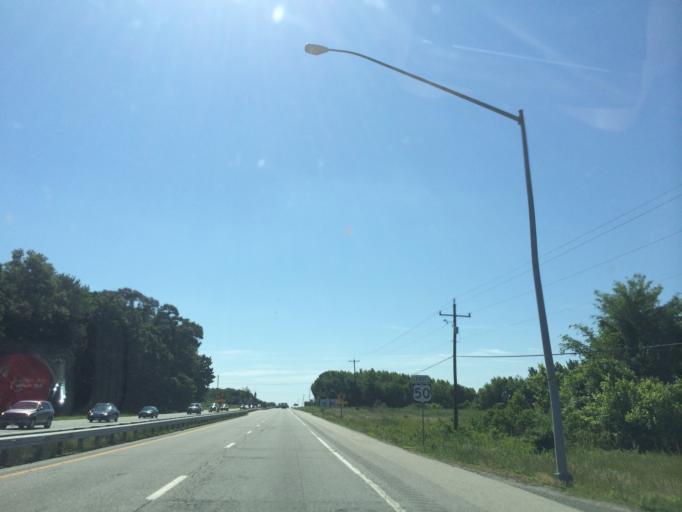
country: US
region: Maryland
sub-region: Queen Anne's County
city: Grasonville
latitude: 38.9800
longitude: -76.1407
